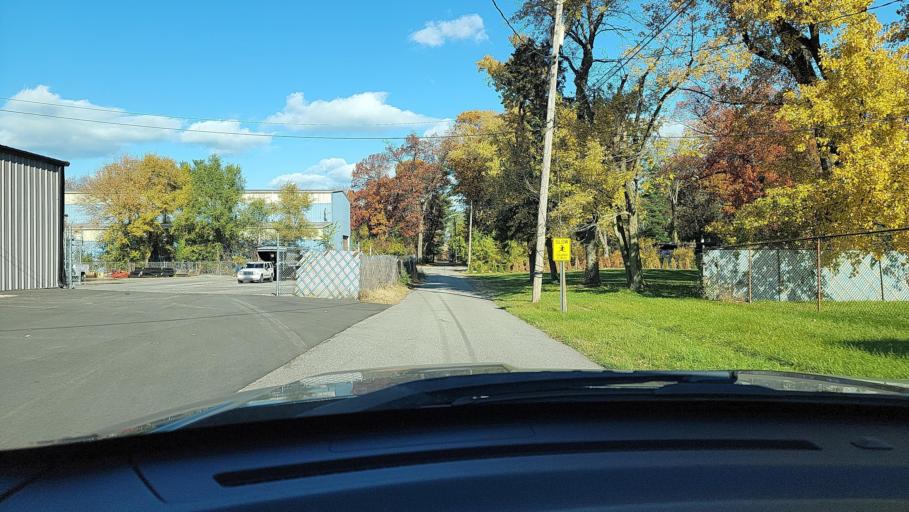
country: US
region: Indiana
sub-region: Porter County
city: Portage
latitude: 41.5991
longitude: -87.1668
